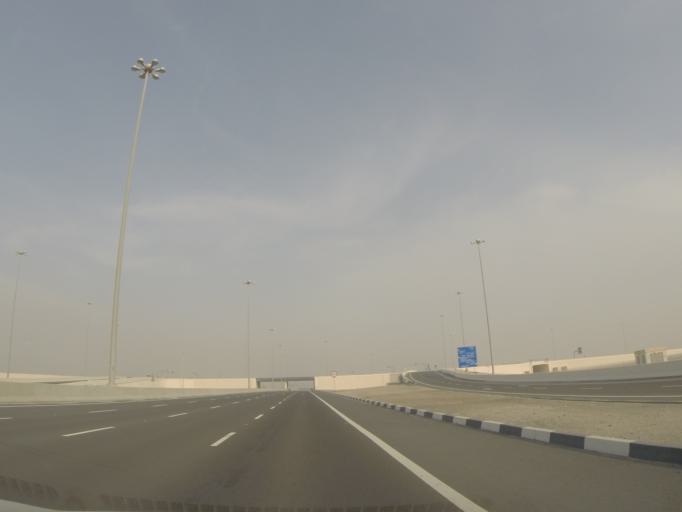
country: AE
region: Abu Dhabi
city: Abu Dhabi
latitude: 24.7720
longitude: 54.7164
